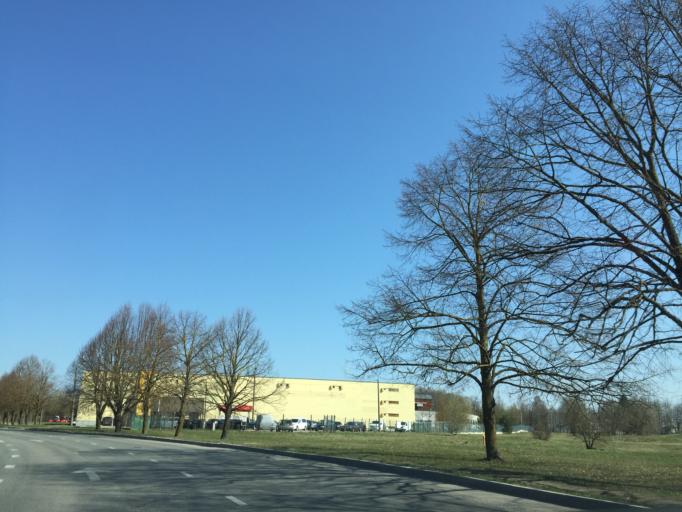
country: EE
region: Tartu
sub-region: Tartu linn
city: Tartu
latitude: 58.3766
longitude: 26.7708
